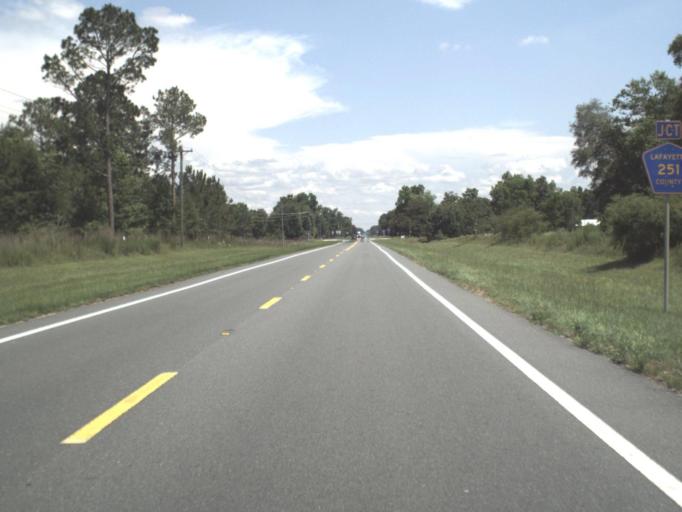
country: US
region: Florida
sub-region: Lafayette County
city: Mayo
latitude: 30.1172
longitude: -83.2603
